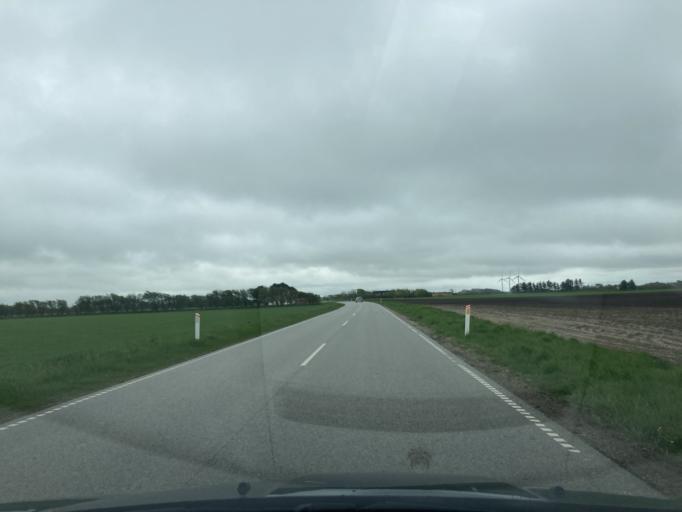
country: DK
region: North Denmark
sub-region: Thisted Kommune
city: Hurup
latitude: 56.8420
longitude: 8.3626
